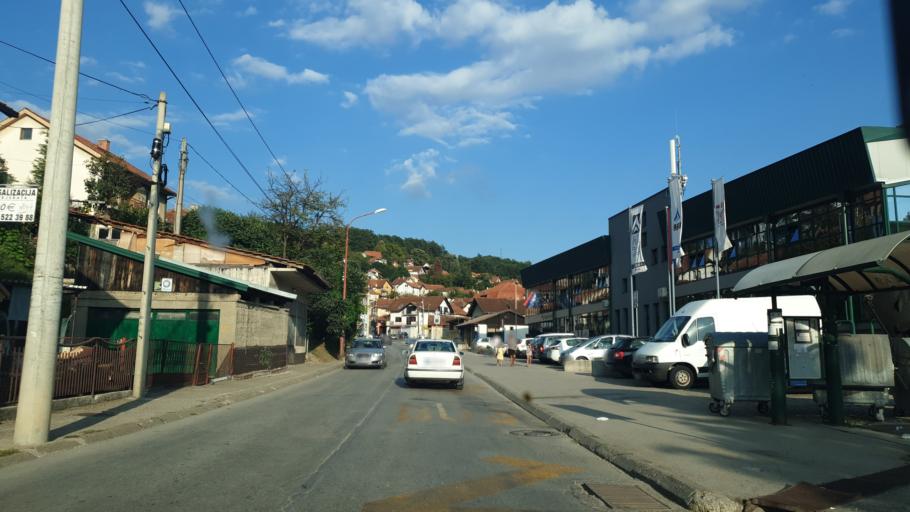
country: RS
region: Central Serbia
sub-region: Zlatiborski Okrug
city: Uzice
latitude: 43.8609
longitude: 19.8555
